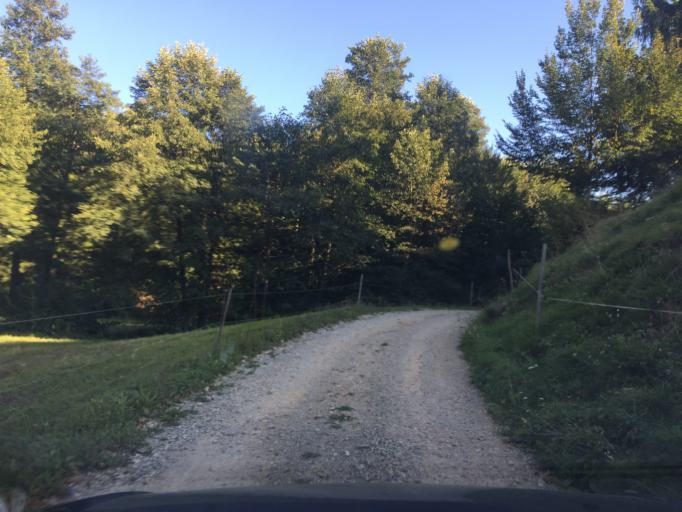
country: SI
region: Postojna
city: Postojna
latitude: 45.8099
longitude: 14.1329
